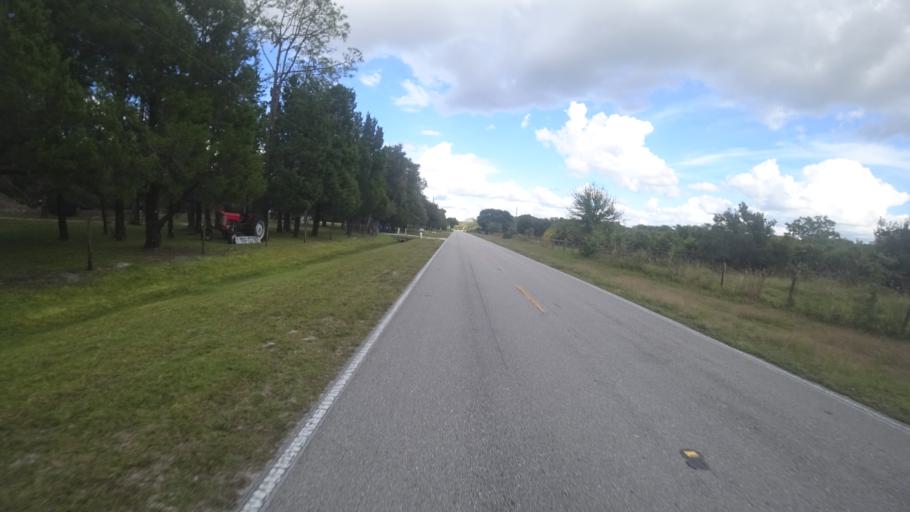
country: US
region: Florida
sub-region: Sarasota County
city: Lake Sarasota
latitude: 27.3420
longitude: -82.1722
